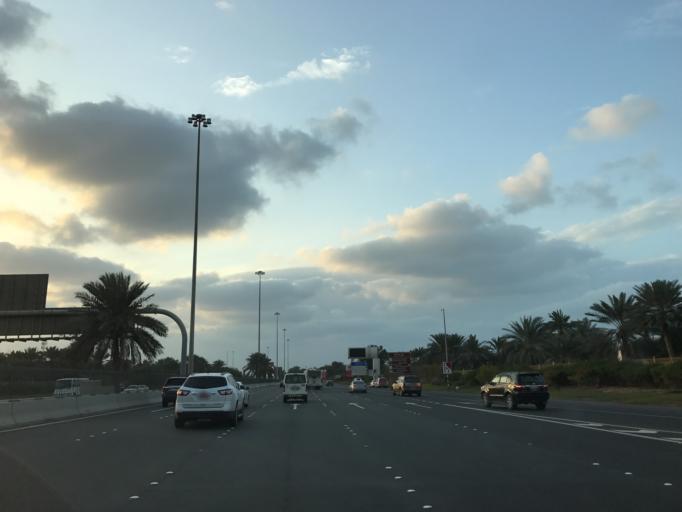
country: AE
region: Abu Dhabi
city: Abu Dhabi
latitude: 24.4188
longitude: 54.4946
